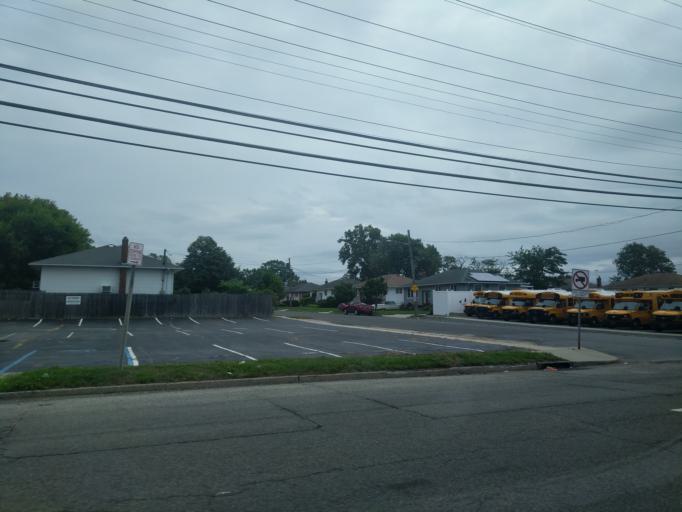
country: US
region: New York
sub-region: Nassau County
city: Oceanside
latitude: 40.6310
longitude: -73.6530
